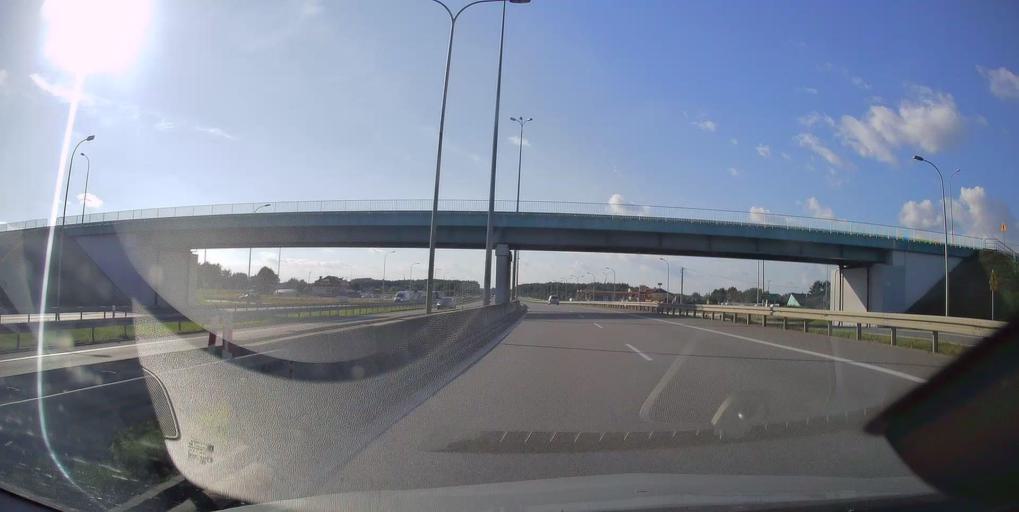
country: PL
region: Masovian Voivodeship
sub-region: Powiat bialobrzeski
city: Stara Blotnica
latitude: 51.5691
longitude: 21.0225
